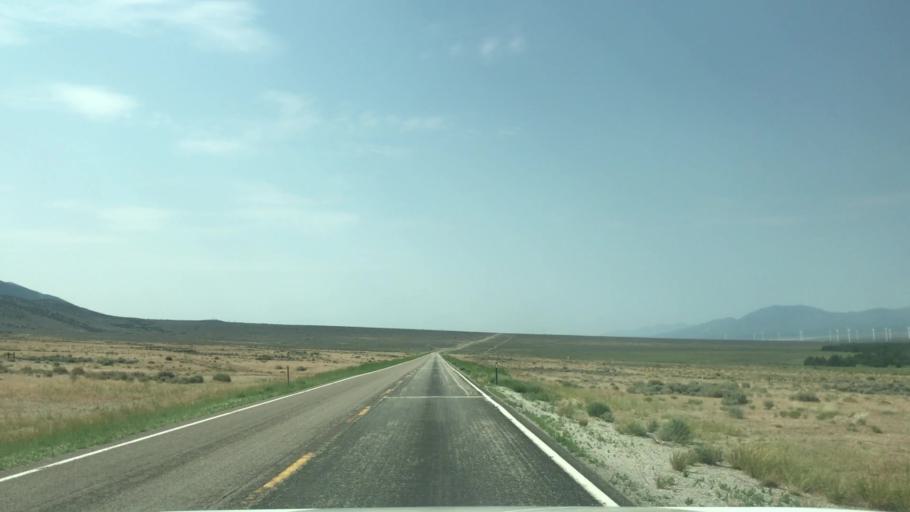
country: US
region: Nevada
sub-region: White Pine County
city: McGill
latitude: 39.1384
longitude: -114.4177
